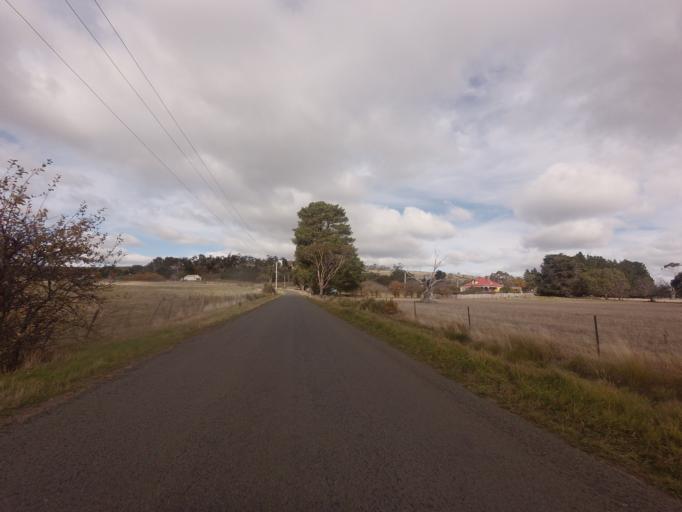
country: AU
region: Tasmania
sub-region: Brighton
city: Bridgewater
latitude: -42.4087
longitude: 147.3976
